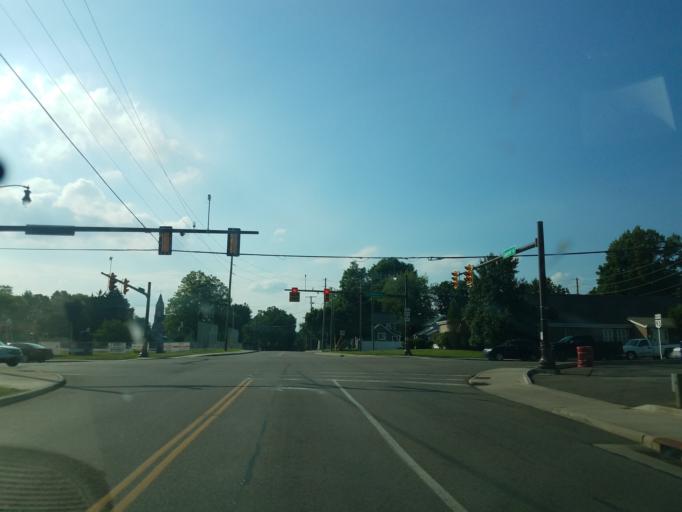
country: US
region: Ohio
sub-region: Stark County
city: Canal Fulton
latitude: 40.8908
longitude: -81.5954
